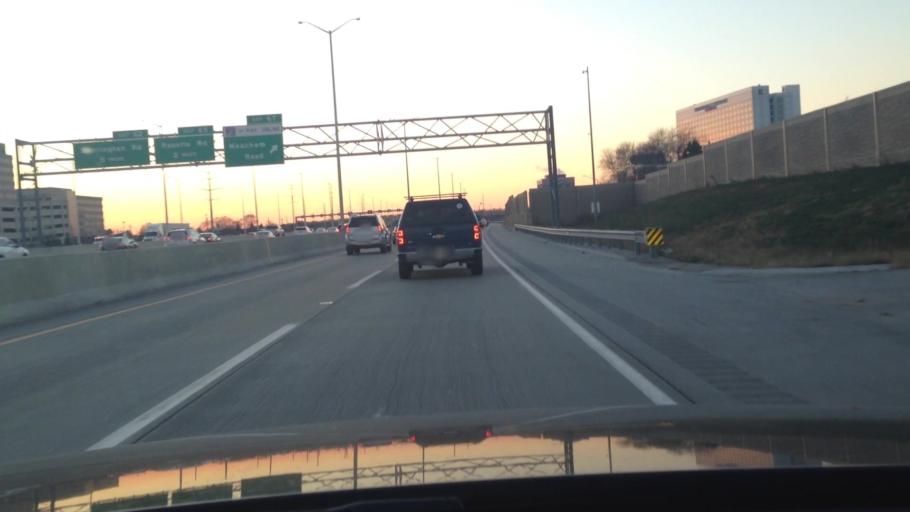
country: US
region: Illinois
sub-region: Cook County
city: Rolling Meadows
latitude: 42.0588
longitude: -88.0359
